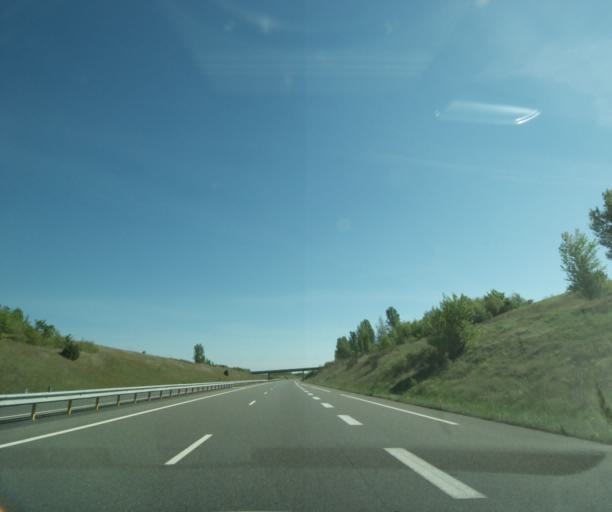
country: FR
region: Midi-Pyrenees
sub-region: Departement du Tarn-et-Garonne
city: Caussade
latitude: 44.2270
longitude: 1.5346
